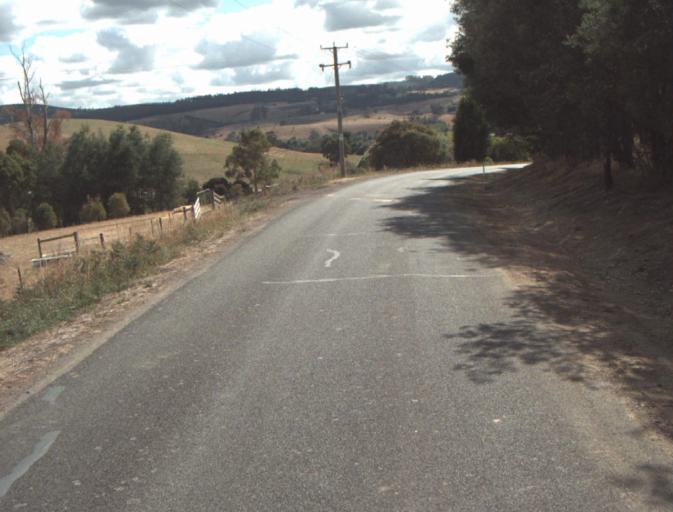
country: AU
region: Tasmania
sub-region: Launceston
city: Mayfield
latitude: -41.2572
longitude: 147.2088
